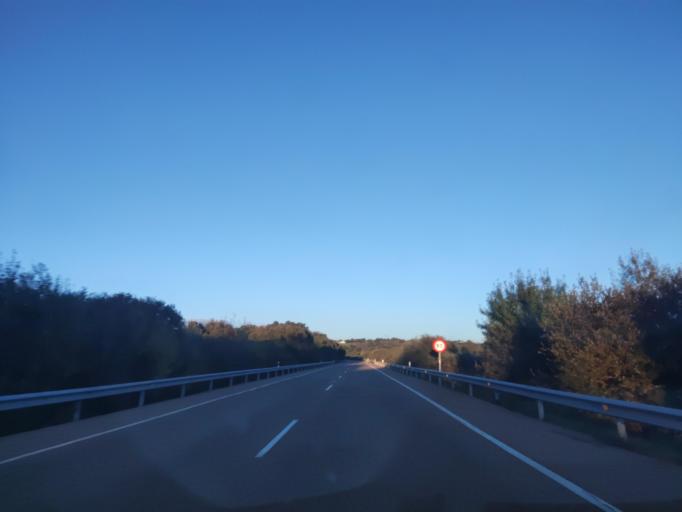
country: ES
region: Castille and Leon
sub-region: Provincia de Salamanca
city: Castraz
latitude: 40.7471
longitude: -6.3433
